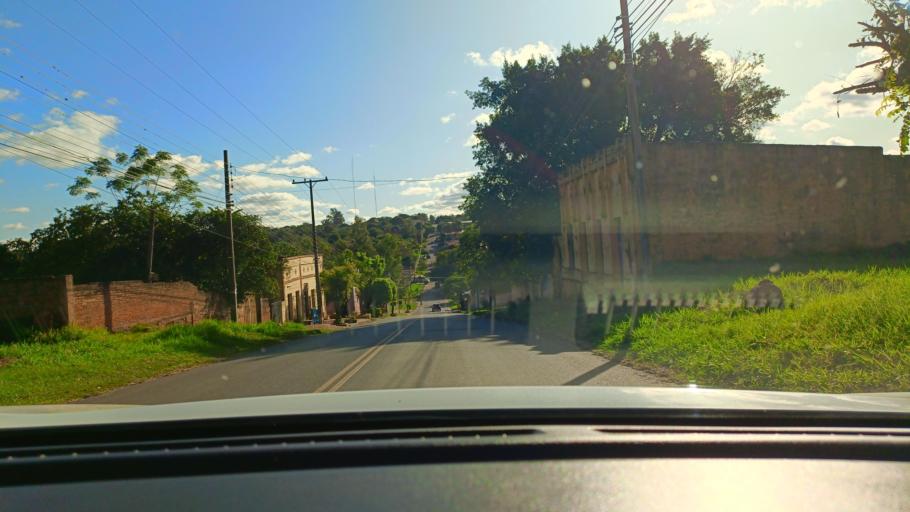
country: PY
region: San Pedro
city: Guayaybi
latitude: -24.6657
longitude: -56.4459
